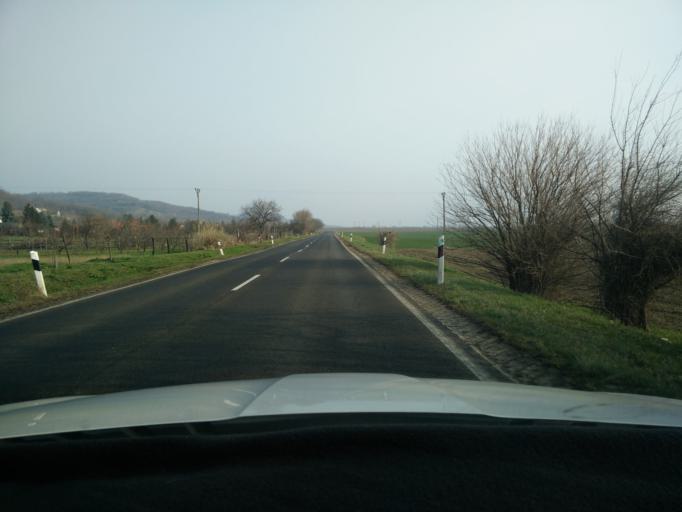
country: HU
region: Tolna
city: Szekszard
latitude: 46.2872
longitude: 18.6852
